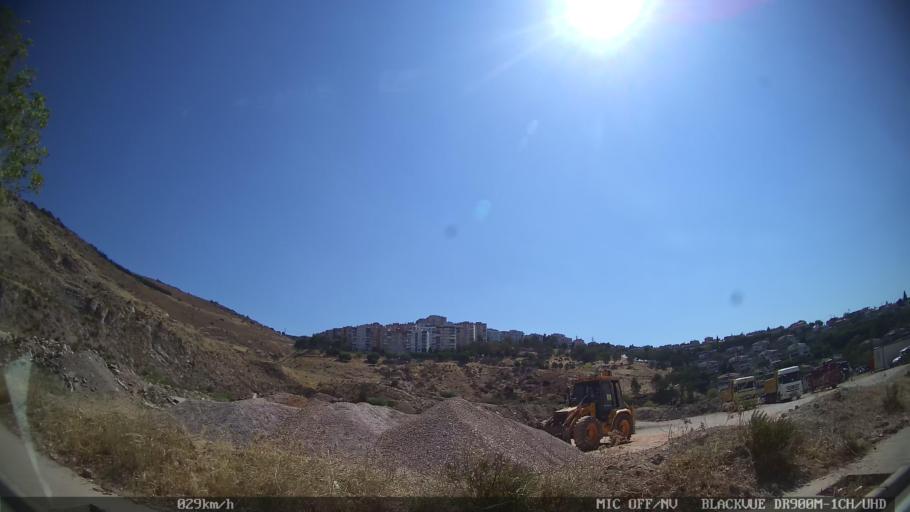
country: TR
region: Izmir
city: Karsiyaka
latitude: 38.5039
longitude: 27.0827
